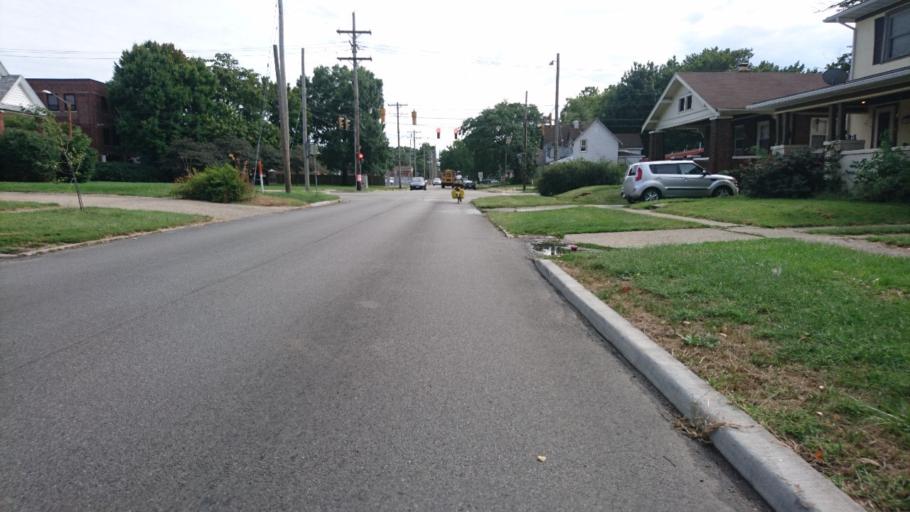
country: US
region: Illinois
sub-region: Sangamon County
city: Southern View
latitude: 39.7797
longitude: -89.6544
